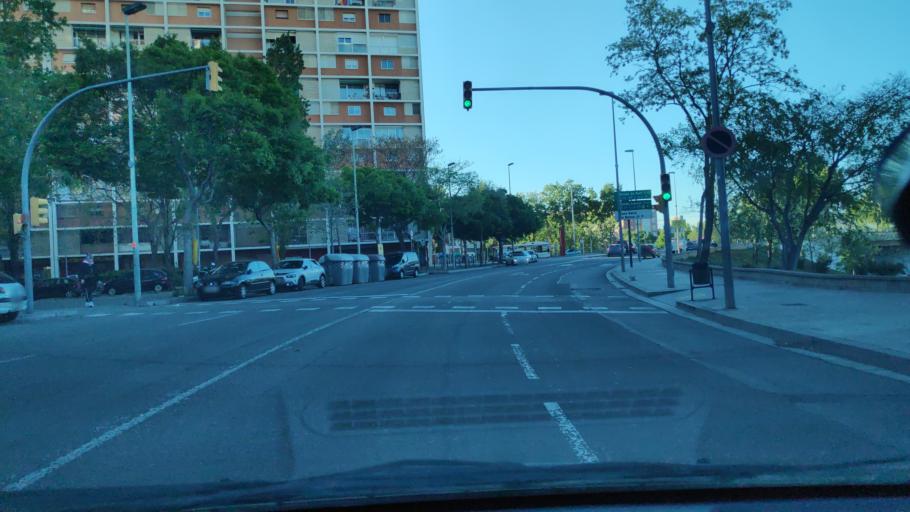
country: ES
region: Catalonia
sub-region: Provincia de Barcelona
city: Sant Adria de Besos
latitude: 41.4243
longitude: 2.2096
